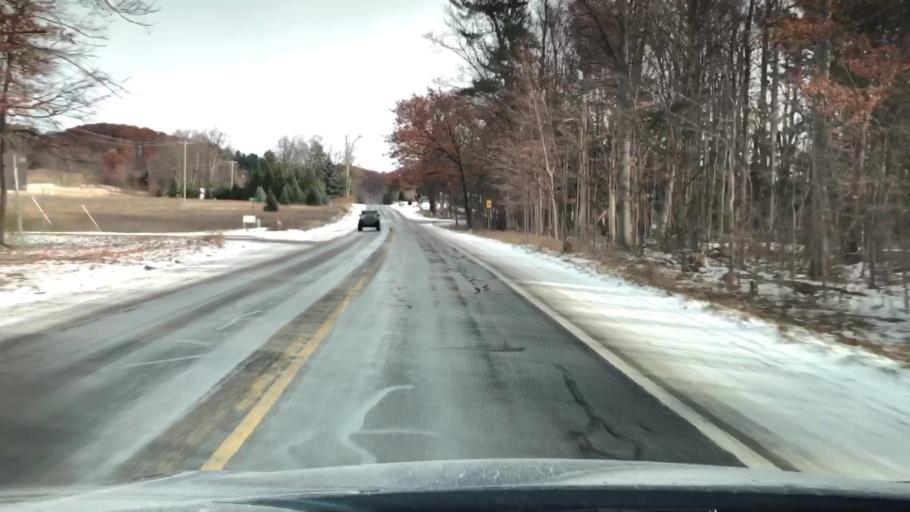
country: US
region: Michigan
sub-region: Grand Traverse County
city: Traverse City
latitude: 44.8375
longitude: -85.5367
